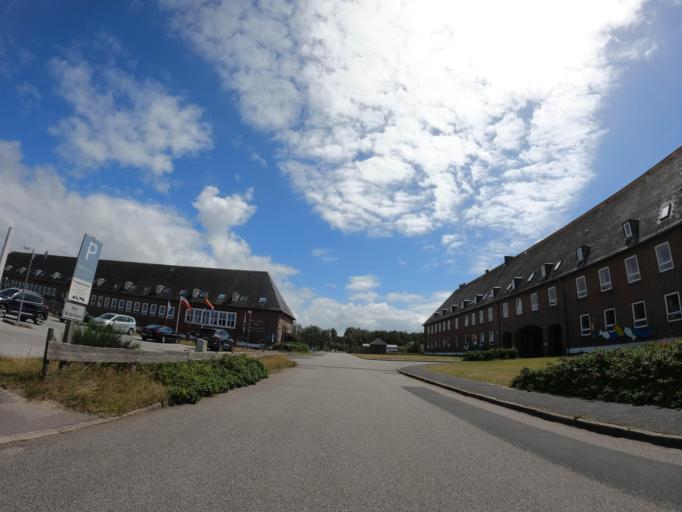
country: DE
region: Schleswig-Holstein
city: Westerland
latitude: 54.8569
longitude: 8.2960
